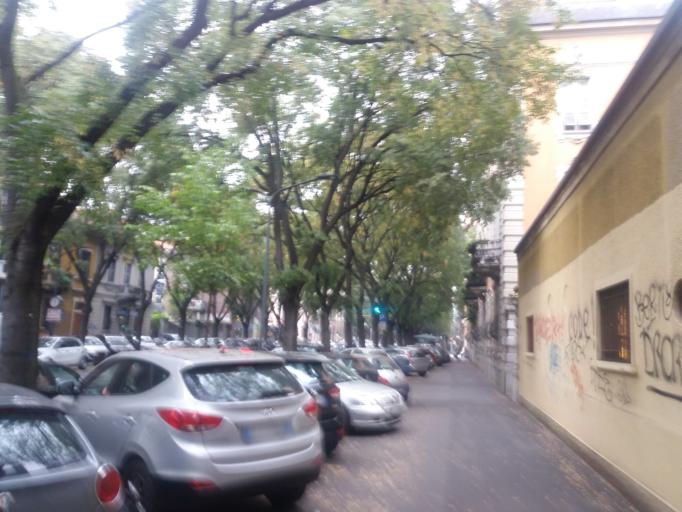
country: IT
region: Lombardy
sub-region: Citta metropolitana di Milano
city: Milano
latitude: 45.4852
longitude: 9.2237
